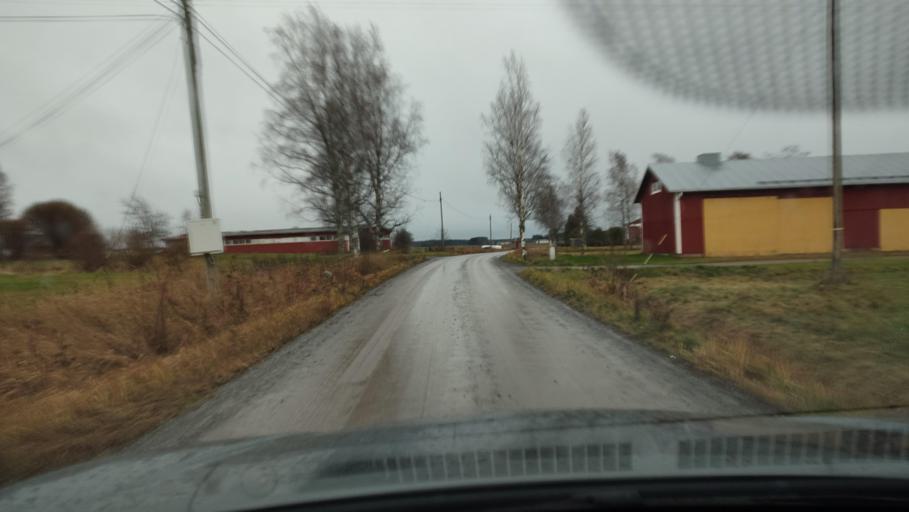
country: FI
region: Southern Ostrobothnia
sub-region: Suupohja
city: Karijoki
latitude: 62.2474
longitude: 21.5482
